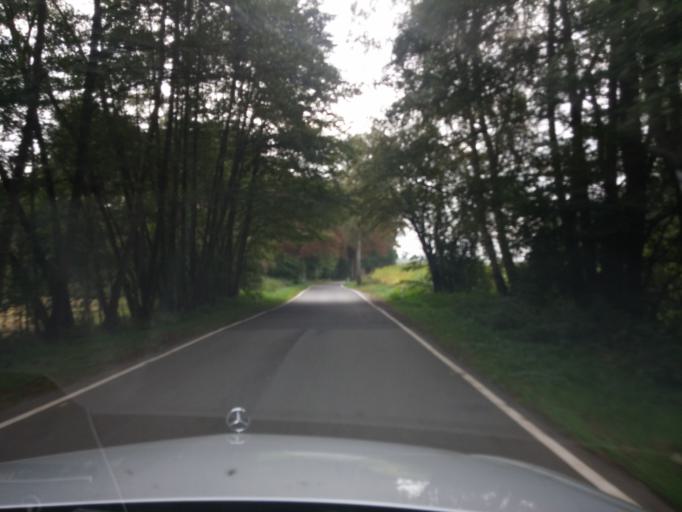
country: DE
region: Brandenburg
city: Putlitz
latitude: 53.2795
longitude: 12.0580
